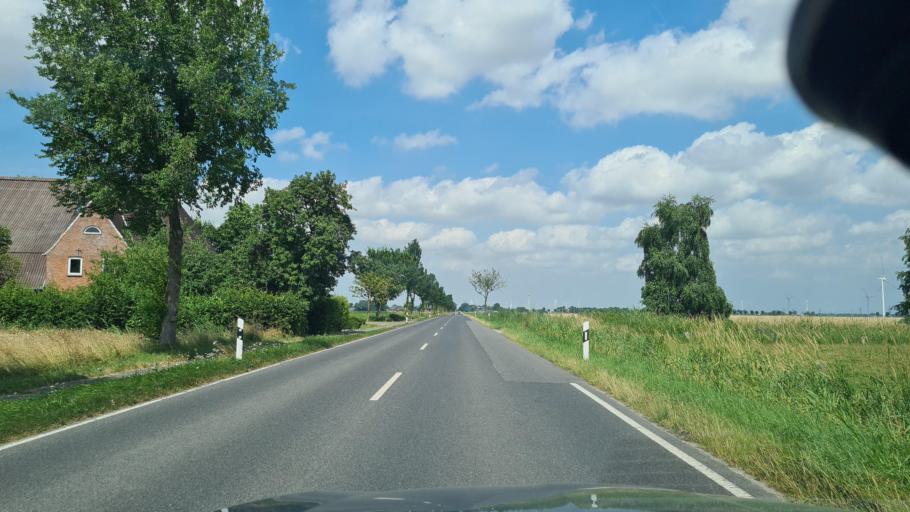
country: DE
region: Schleswig-Holstein
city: Epenwohrden
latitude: 54.1322
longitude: 9.0167
